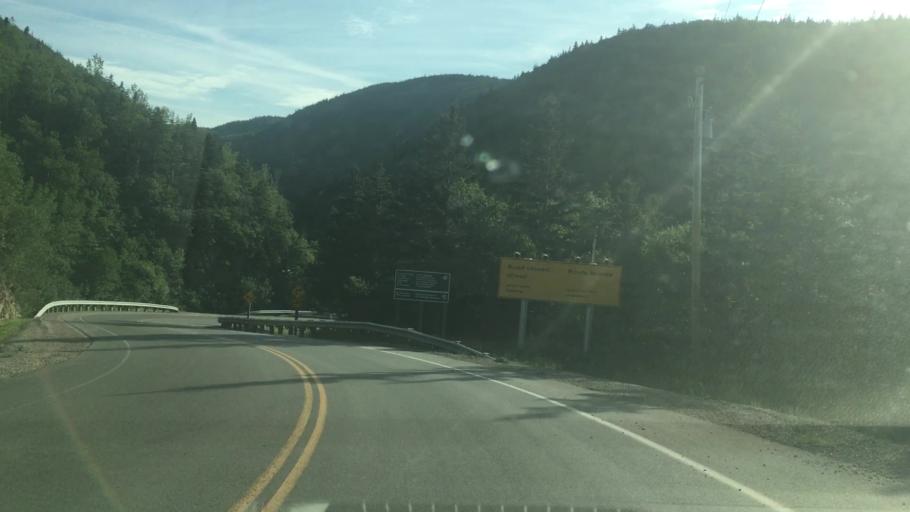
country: CA
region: Nova Scotia
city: Sydney Mines
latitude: 46.8224
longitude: -60.8270
